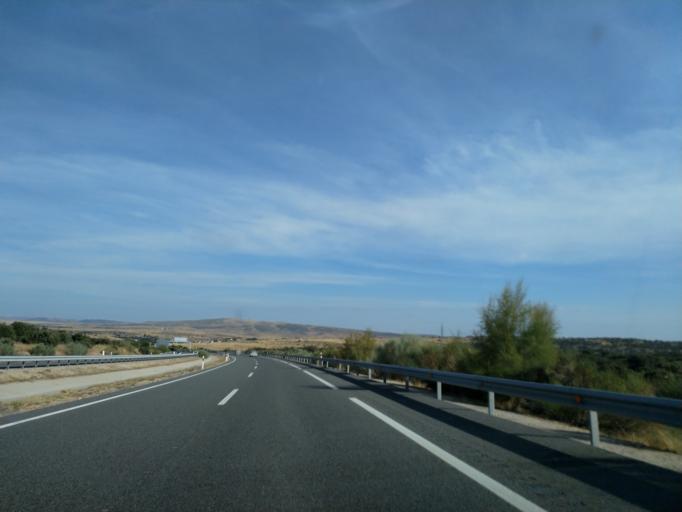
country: ES
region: Castille and Leon
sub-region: Provincia de Avila
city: Berrocalejo de Aragona
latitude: 40.6761
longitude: -4.6255
